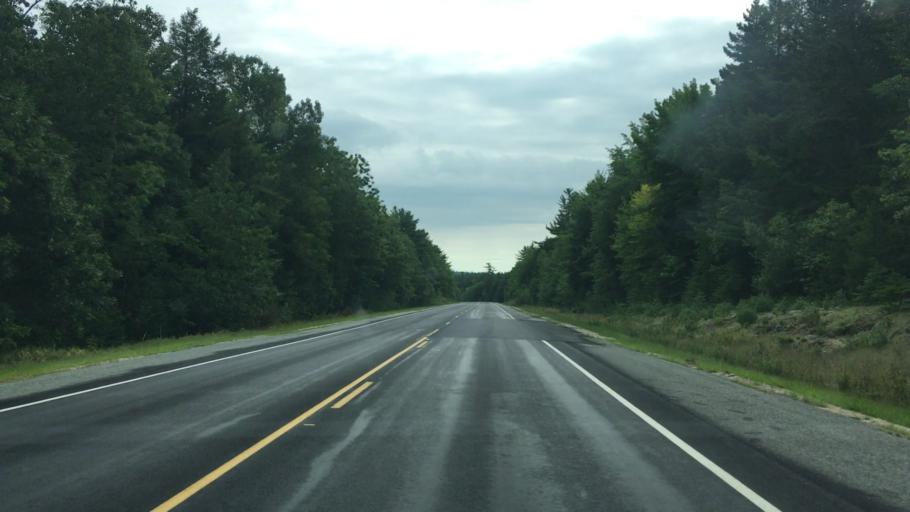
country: US
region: Maine
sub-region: Washington County
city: Addison
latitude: 44.9099
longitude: -67.8486
